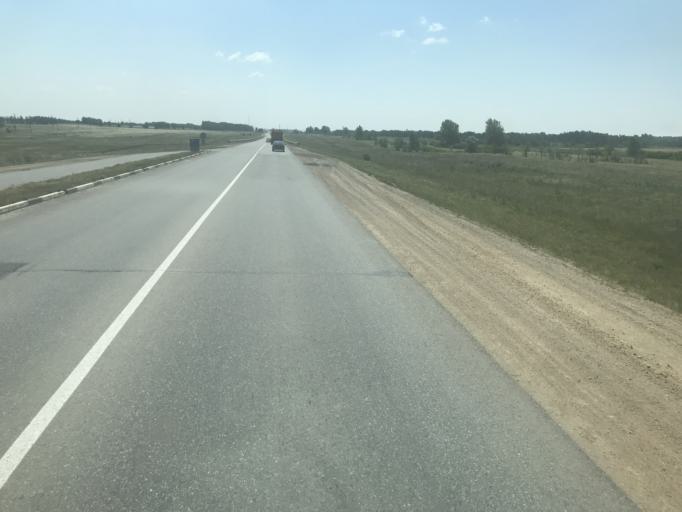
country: KZ
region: Aqmola
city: Kokshetau
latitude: 53.4126
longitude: 69.4261
